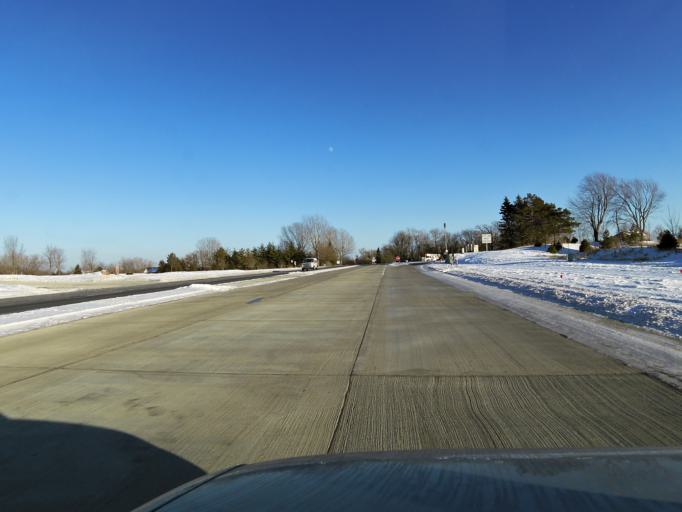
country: US
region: Minnesota
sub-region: Scott County
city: Shakopee
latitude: 44.7612
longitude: -93.5075
